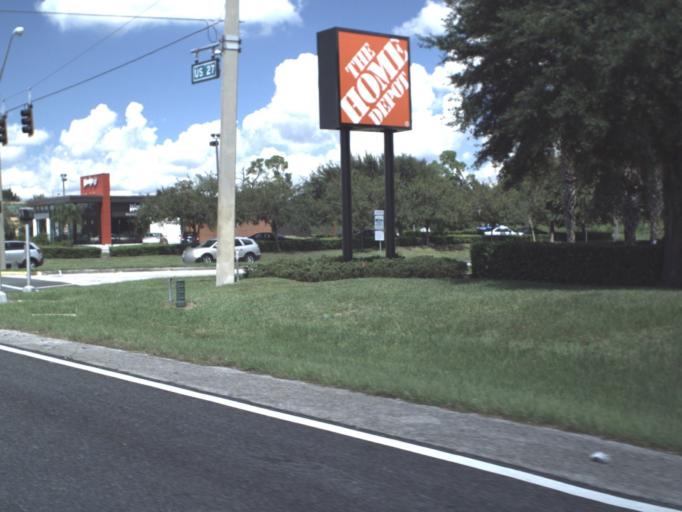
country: US
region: Florida
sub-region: Polk County
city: Dundee
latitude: 27.9631
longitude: -81.6251
